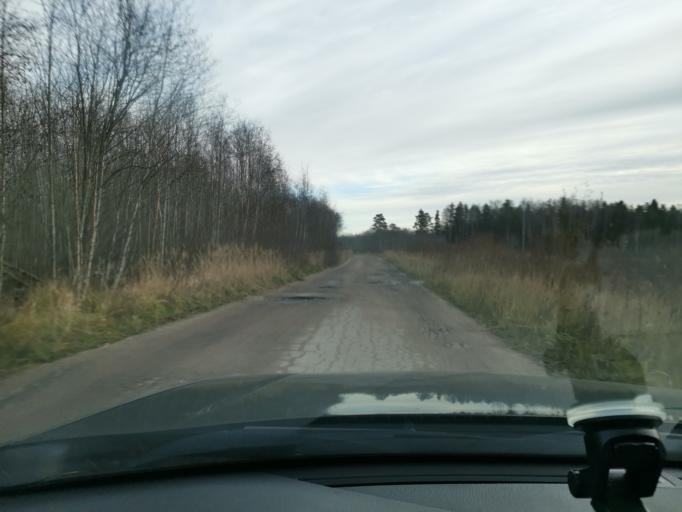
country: EE
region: Ida-Virumaa
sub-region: Sillamaee linn
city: Sillamae
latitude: 59.2593
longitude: 27.9119
